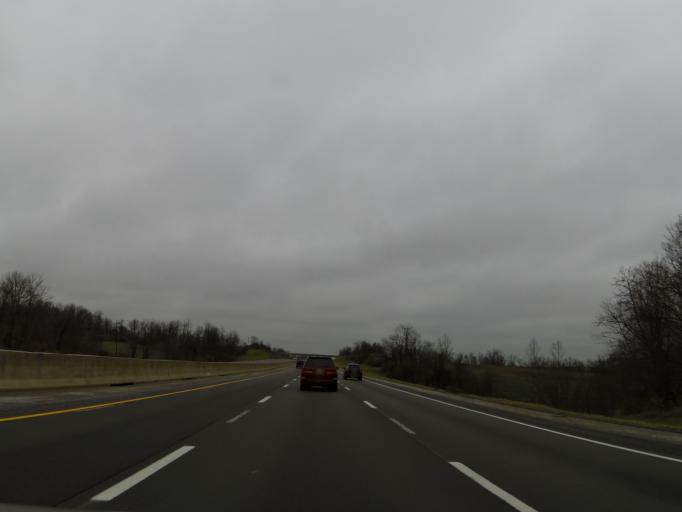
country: US
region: Kentucky
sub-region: Grant County
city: Crittenden
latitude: 38.7378
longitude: -84.6050
